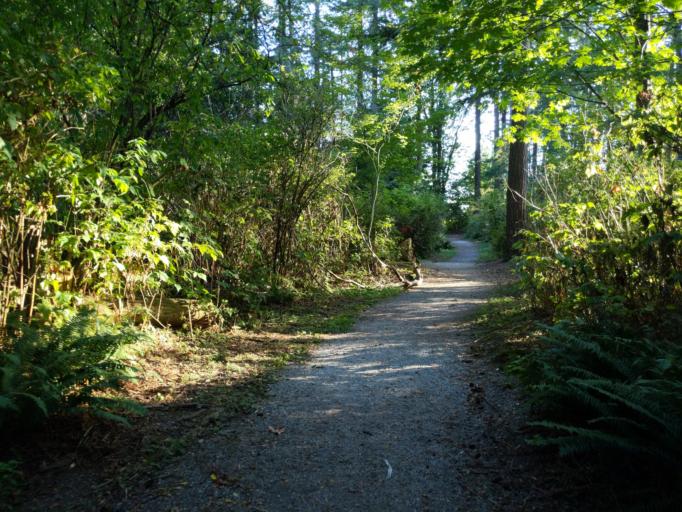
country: CA
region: British Columbia
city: New Westminster
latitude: 49.1943
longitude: -122.8637
